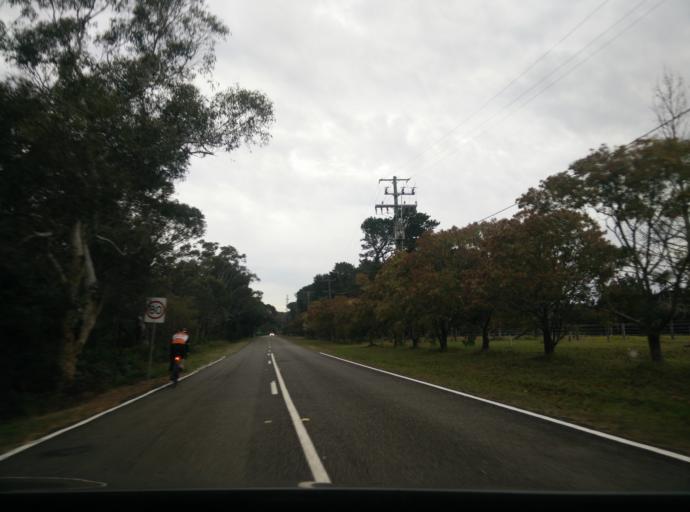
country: AU
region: New South Wales
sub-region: Gosford Shire
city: Narara
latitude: -33.3503
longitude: 151.2901
